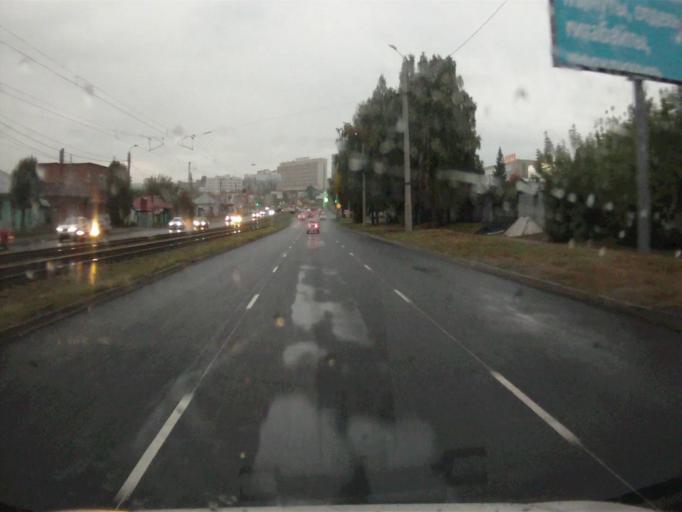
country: RU
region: Chelyabinsk
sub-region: Gorod Chelyabinsk
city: Chelyabinsk
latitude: 55.1866
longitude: 61.3643
